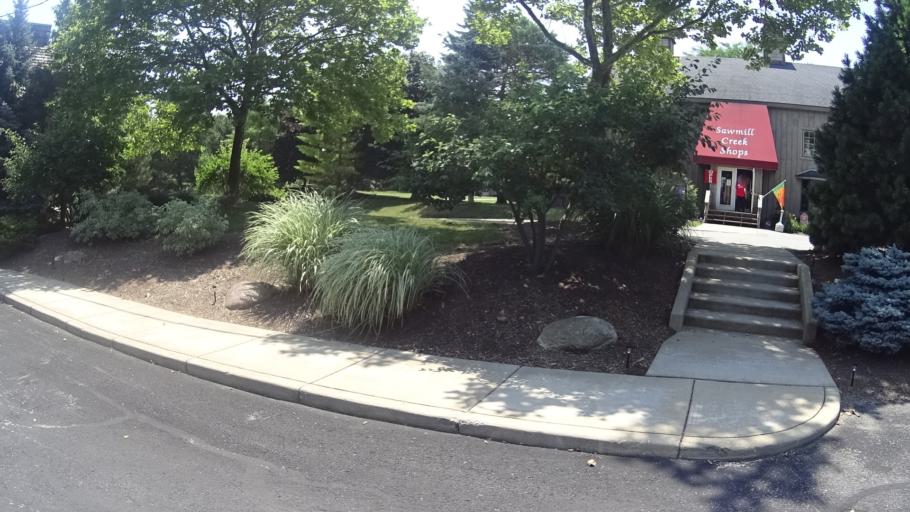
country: US
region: Ohio
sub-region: Erie County
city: Huron
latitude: 41.4080
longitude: -82.5967
